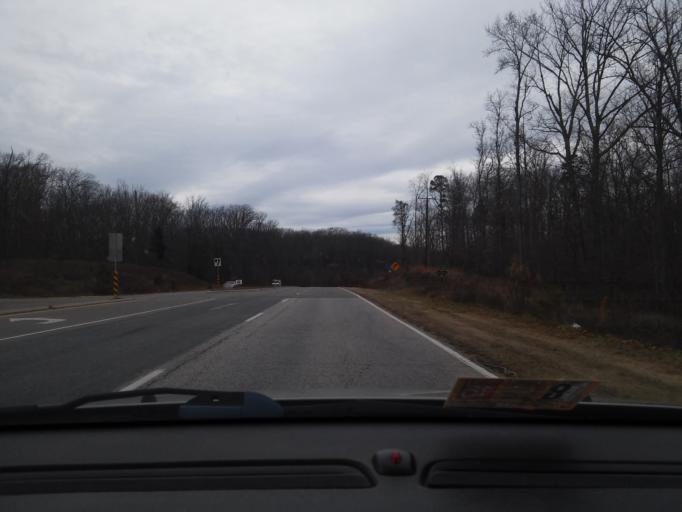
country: US
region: Virginia
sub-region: Chesterfield County
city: Bon Air
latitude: 37.5421
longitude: -77.6467
